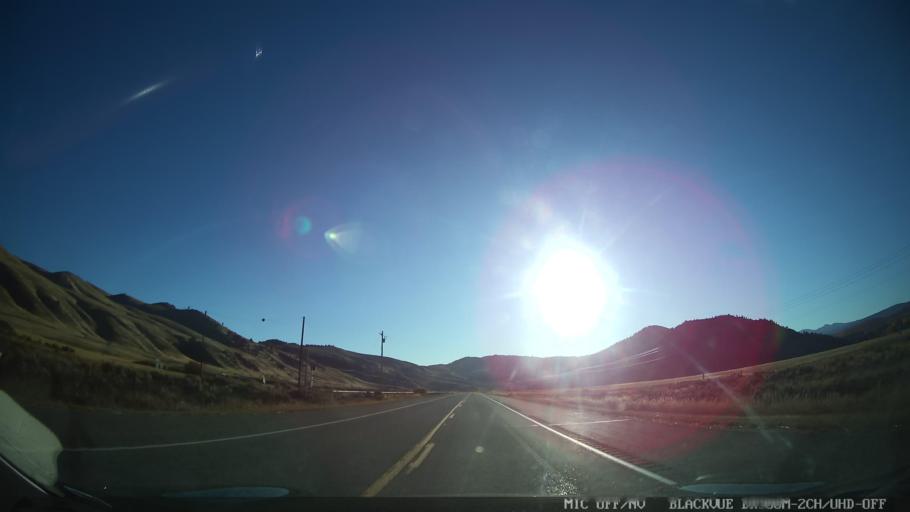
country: US
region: Colorado
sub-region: Grand County
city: Hot Sulphur Springs
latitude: 40.0518
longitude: -106.1527
